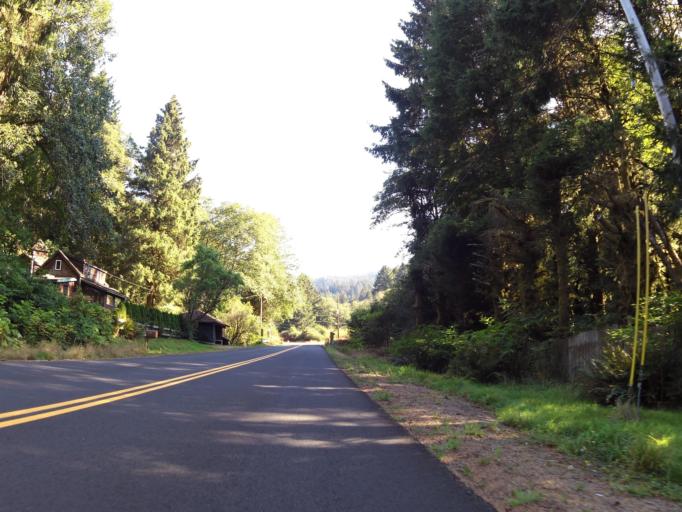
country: US
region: Oregon
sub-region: Lincoln County
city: Rose Lodge
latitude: 45.0816
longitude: -123.9448
